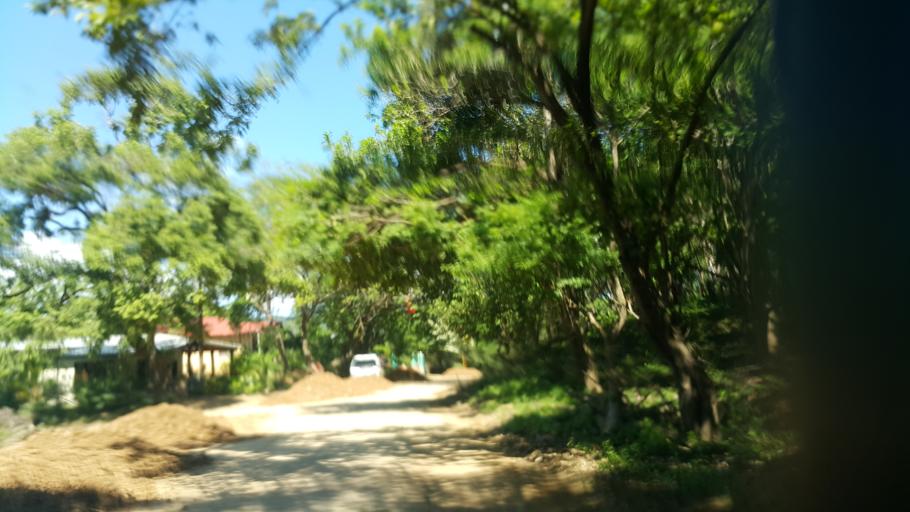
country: NI
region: Rivas
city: San Juan del Sur
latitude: 11.2908
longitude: -85.8903
